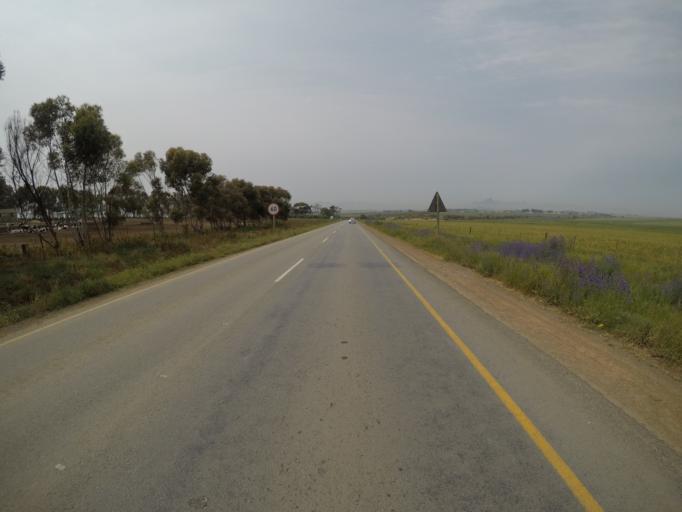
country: ZA
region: Western Cape
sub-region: City of Cape Town
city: Kraaifontein
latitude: -33.7072
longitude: 18.6934
